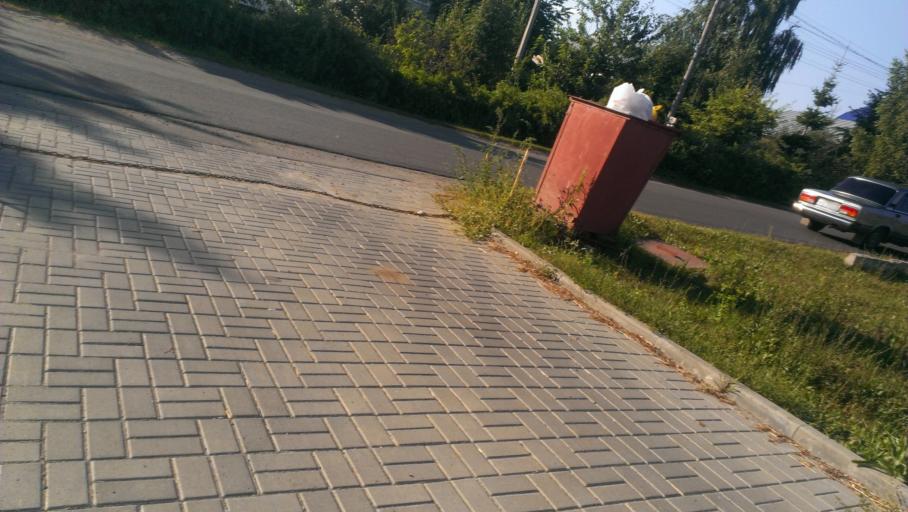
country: RU
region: Altai Krai
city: Novosilikatnyy
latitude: 53.3588
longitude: 83.6393
